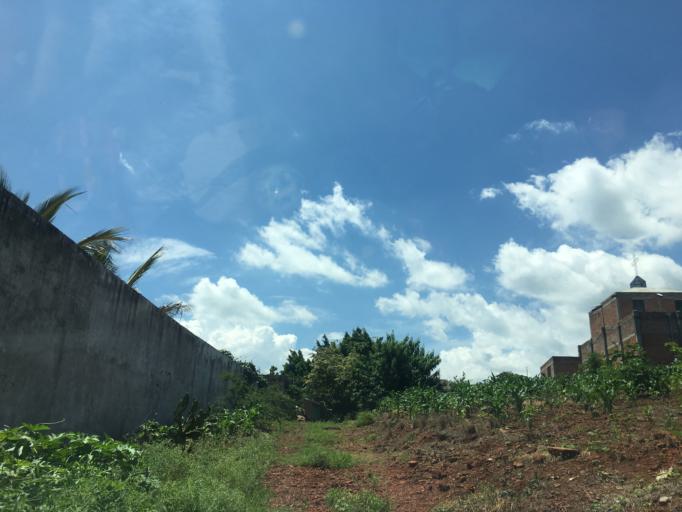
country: MX
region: Nayarit
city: Ixtlan del Rio
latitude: 21.0340
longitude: -104.3525
